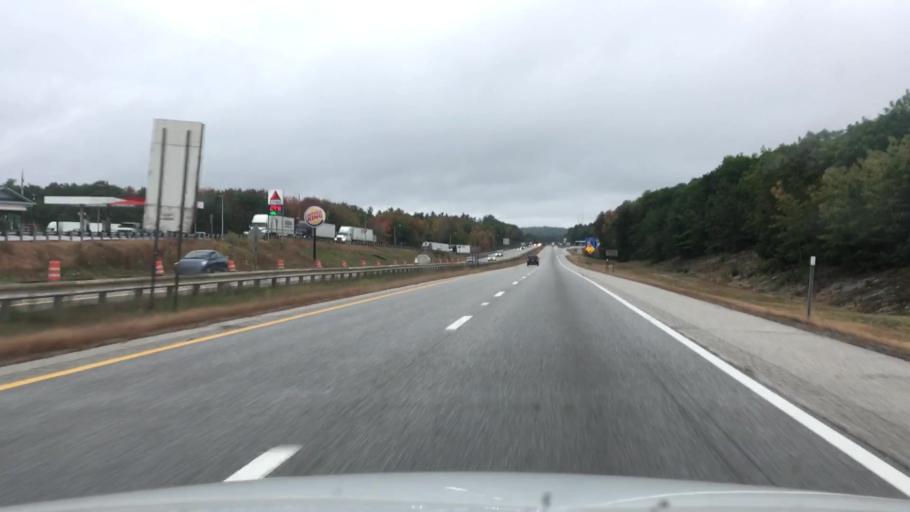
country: US
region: Maine
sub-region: Cumberland County
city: Cumberland Center
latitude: 43.8168
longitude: -70.3186
